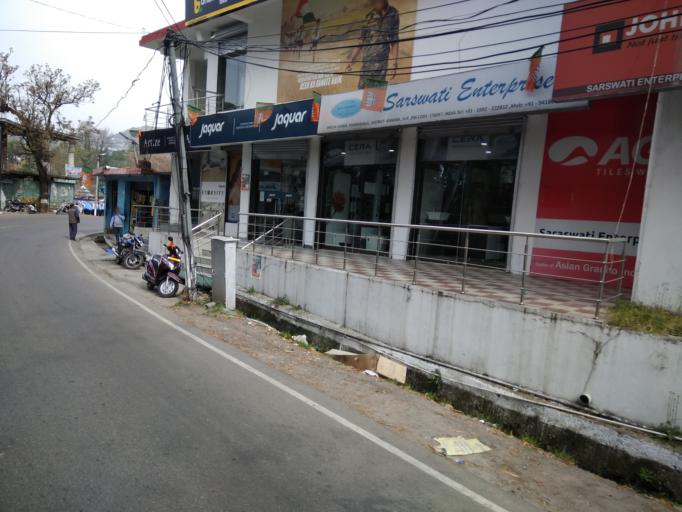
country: IN
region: Himachal Pradesh
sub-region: Kangra
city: Dharmsala
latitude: 32.1964
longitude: 76.3439
